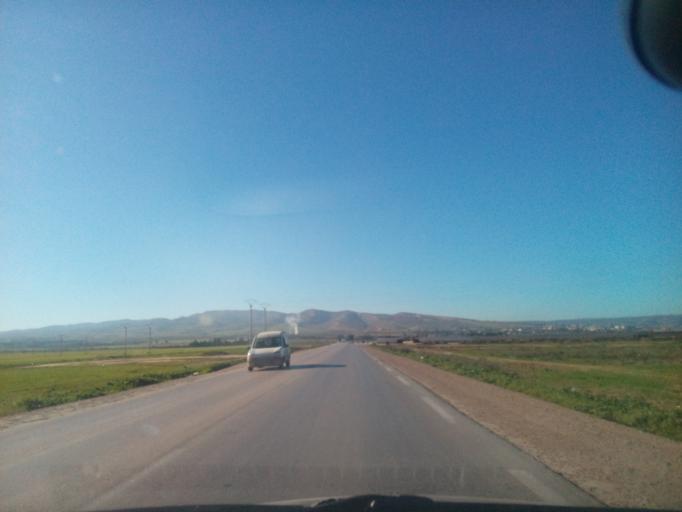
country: DZ
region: Relizane
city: Relizane
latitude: 35.8976
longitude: 0.5506
